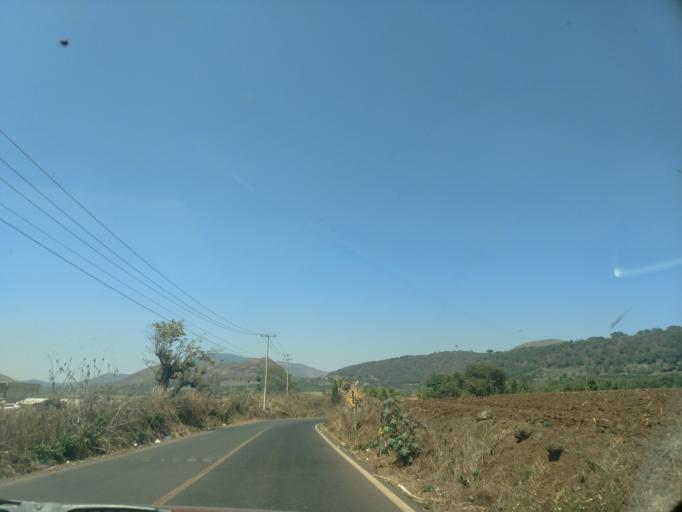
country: MX
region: Nayarit
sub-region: Tepic
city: La Corregidora
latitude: 21.4932
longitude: -104.7902
